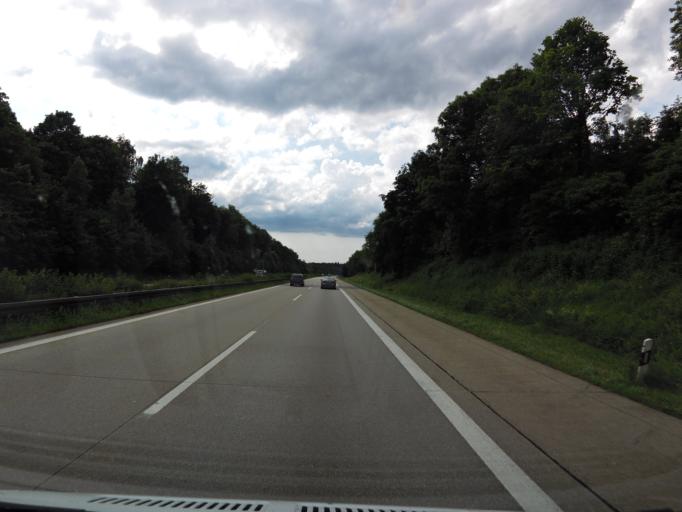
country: DE
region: Bavaria
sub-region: Lower Bavaria
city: Winzer
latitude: 48.7525
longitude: 13.0818
